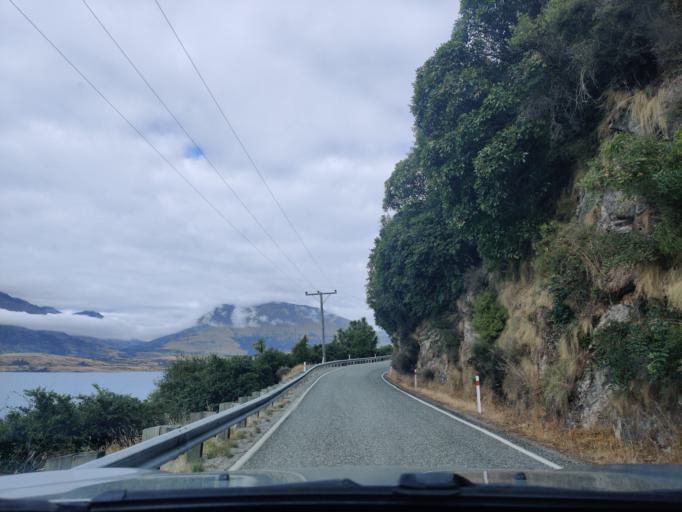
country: NZ
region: Otago
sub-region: Queenstown-Lakes District
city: Queenstown
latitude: -45.0802
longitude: 168.4799
